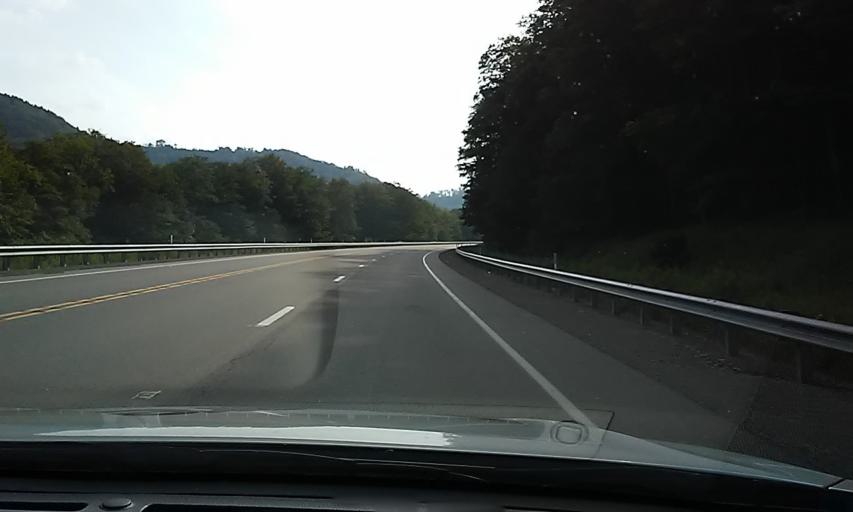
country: US
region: Pennsylvania
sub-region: Potter County
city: Coudersport
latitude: 41.7748
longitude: -77.8361
